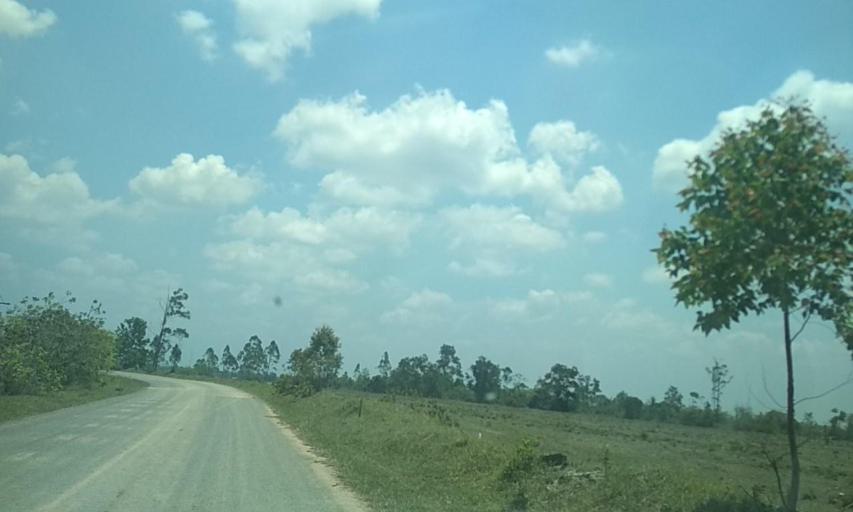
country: MX
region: Tabasco
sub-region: Huimanguillo
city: Francisco Rueda
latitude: 17.8091
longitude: -93.8677
